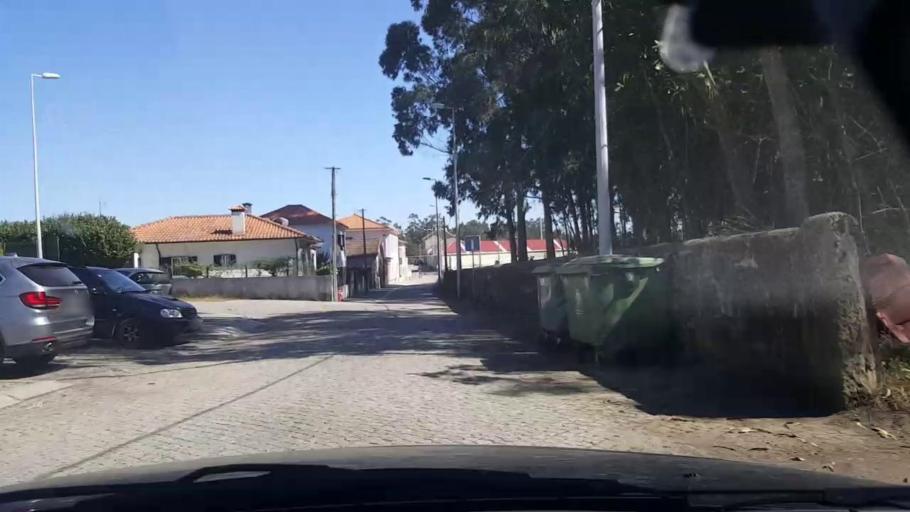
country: PT
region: Porto
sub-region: Matosinhos
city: Lavra
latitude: 41.2841
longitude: -8.6946
